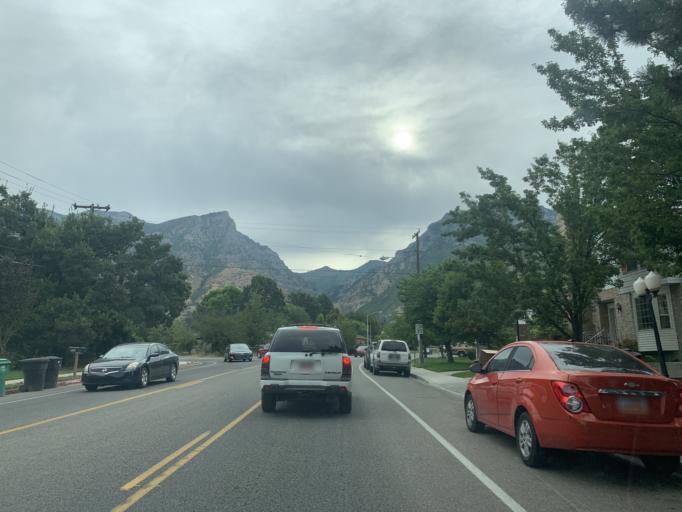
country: US
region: Utah
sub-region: Utah County
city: Provo
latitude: 40.2634
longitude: -111.6546
